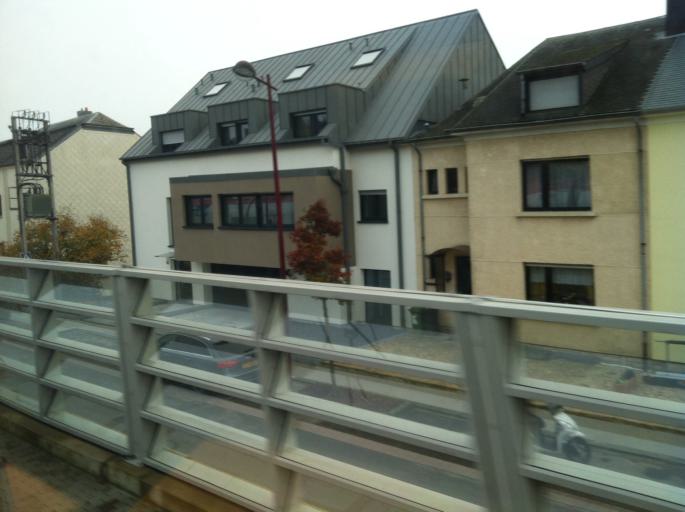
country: LU
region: Luxembourg
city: Bergem
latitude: 49.5081
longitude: 6.0527
